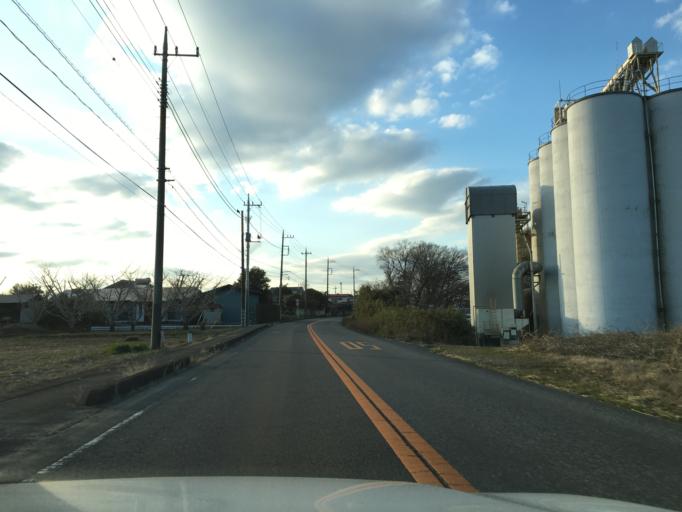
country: JP
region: Tochigi
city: Otawara
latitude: 36.8671
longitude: 140.0794
